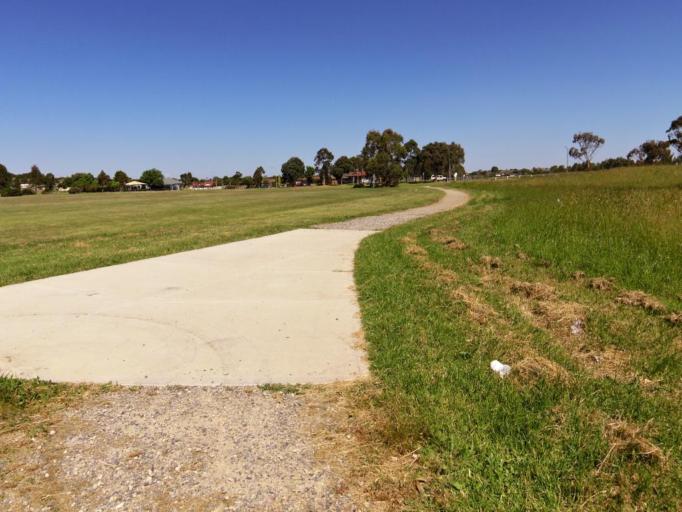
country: AU
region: Victoria
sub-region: Casey
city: Narre Warren South
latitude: -38.0458
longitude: 145.2888
